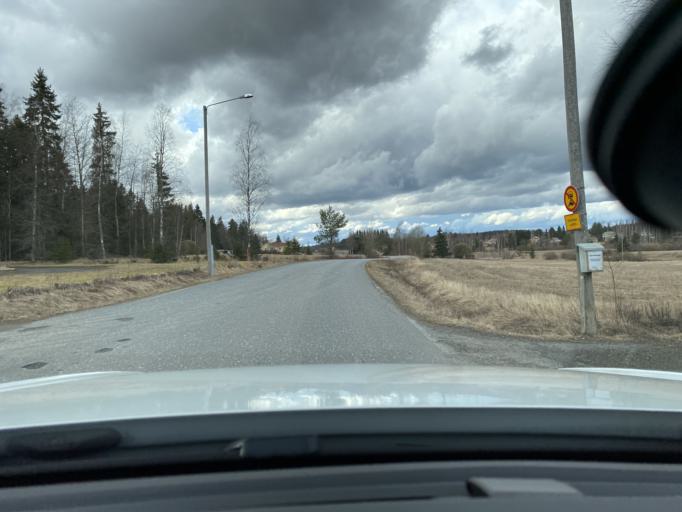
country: FI
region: Pirkanmaa
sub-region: Lounais-Pirkanmaa
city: Punkalaidun
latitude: 61.1118
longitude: 23.0931
